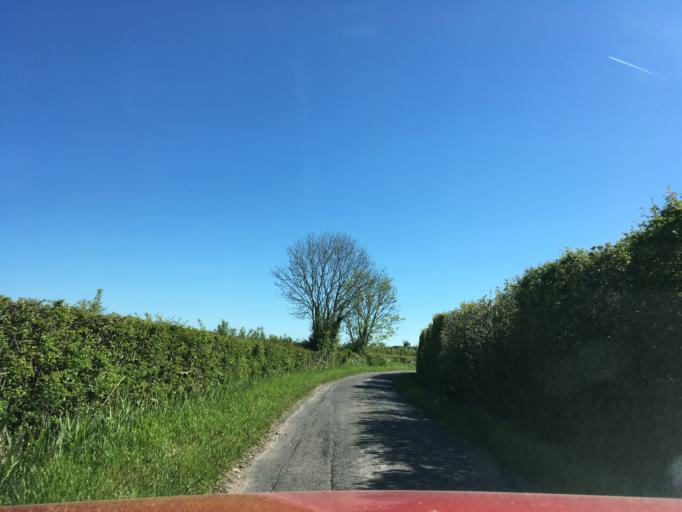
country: GB
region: England
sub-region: South Gloucestershire
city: Severn Beach
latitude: 51.5824
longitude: -2.6171
